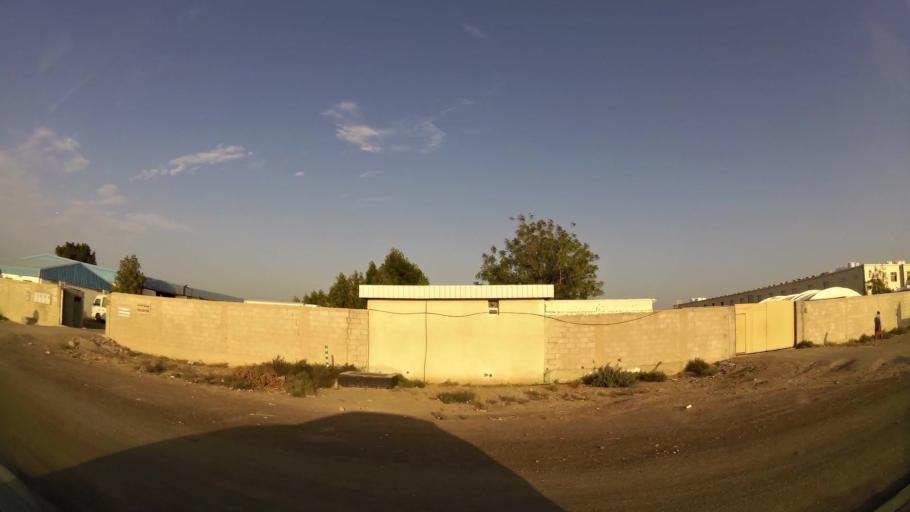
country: AE
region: Abu Dhabi
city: Al Ain
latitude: 24.1530
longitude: 55.8397
